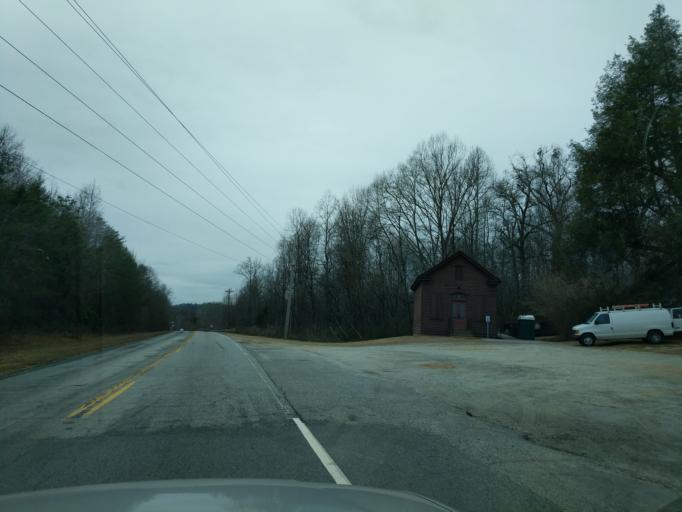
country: US
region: South Carolina
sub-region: Greenville County
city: Slater-Marietta
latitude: 35.0885
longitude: -82.4510
